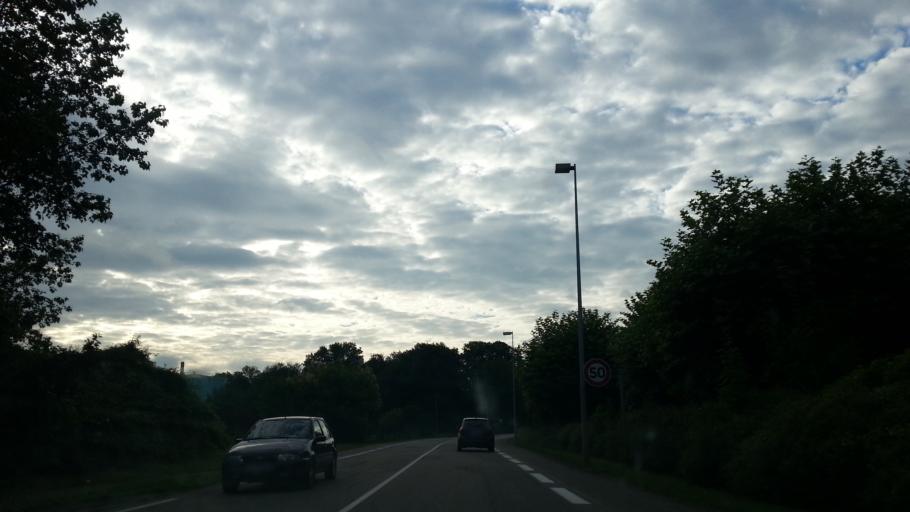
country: FR
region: Alsace
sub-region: Departement du Bas-Rhin
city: Erstein
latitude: 48.4087
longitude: 7.6860
